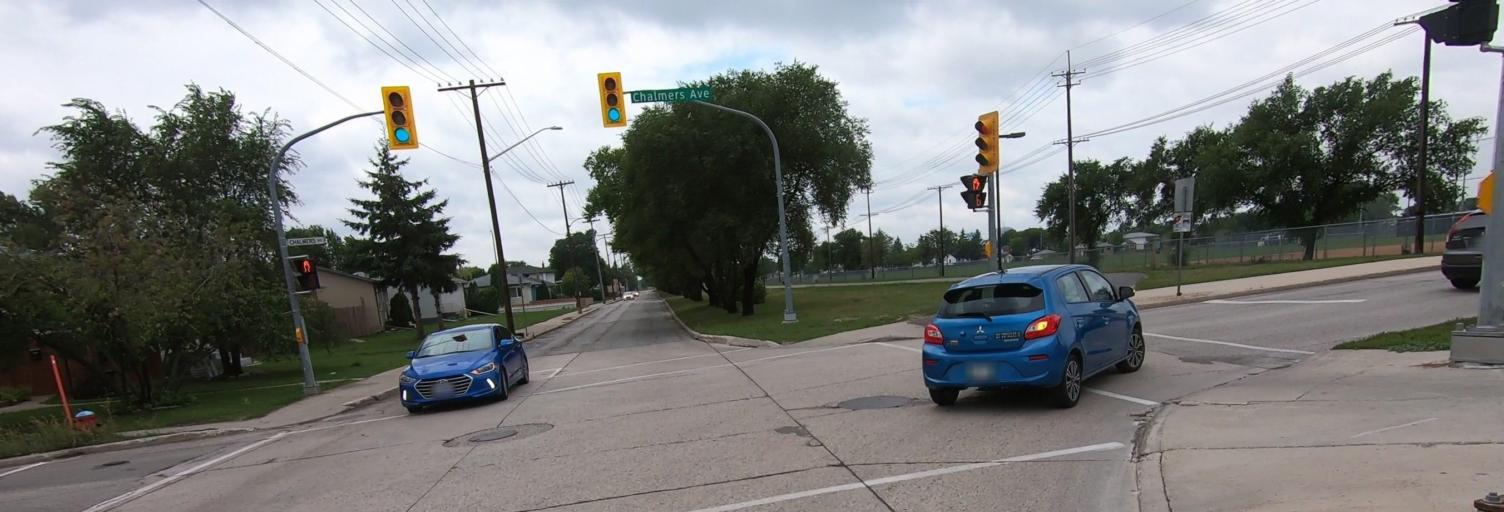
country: CA
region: Manitoba
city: Winnipeg
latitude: 49.9093
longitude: -97.0962
